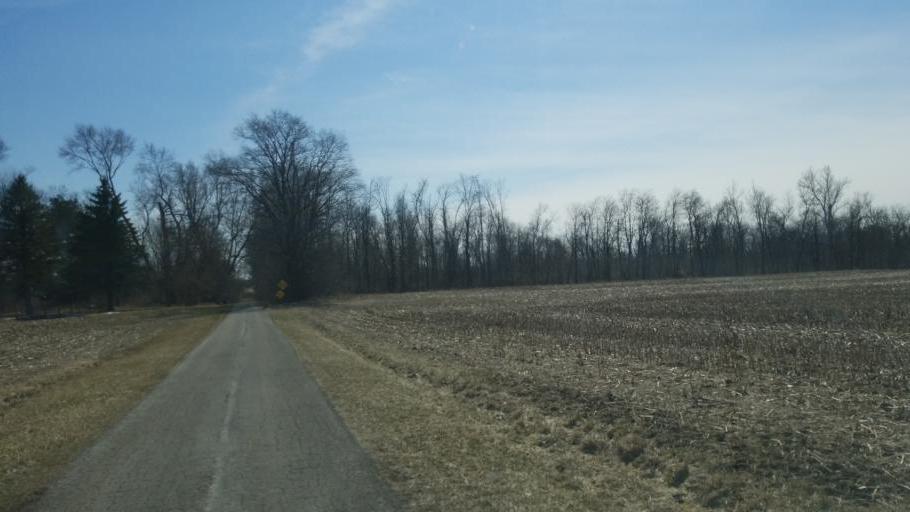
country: US
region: Ohio
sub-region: Morrow County
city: Cardington
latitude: 40.6353
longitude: -82.9425
